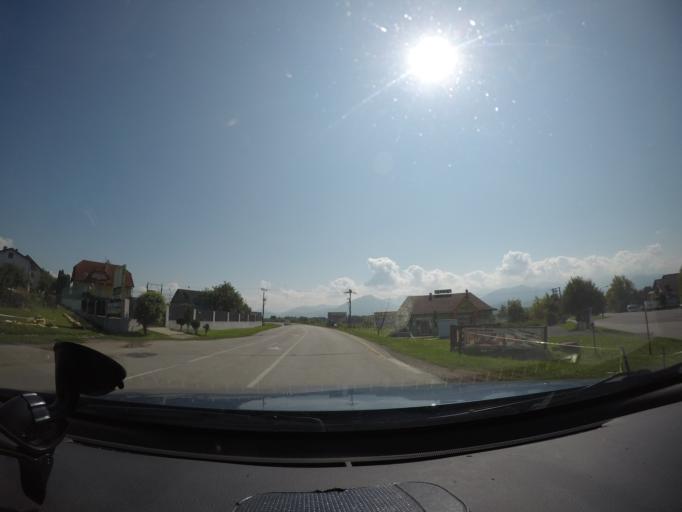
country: SK
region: Zilinsky
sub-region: Okres Liptovsky Mikulas
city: Liptovsky Mikulas
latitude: 49.1130
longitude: 19.5464
